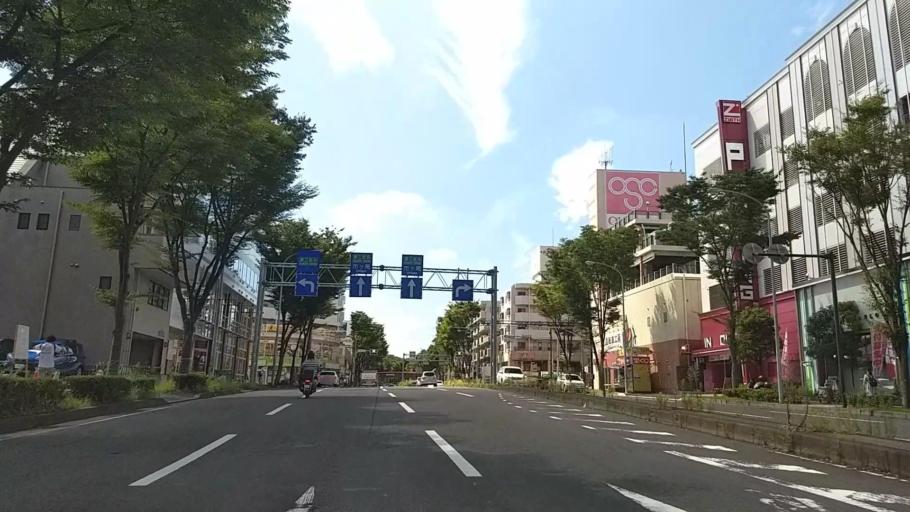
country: JP
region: Tokyo
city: Chofugaoka
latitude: 35.5436
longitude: 139.5705
